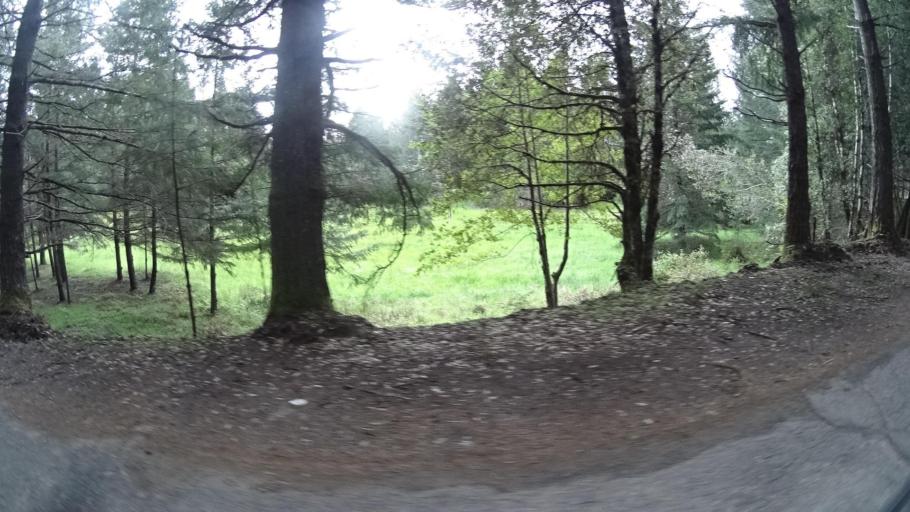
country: US
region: California
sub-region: Humboldt County
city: Redway
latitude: 40.2355
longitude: -123.7621
